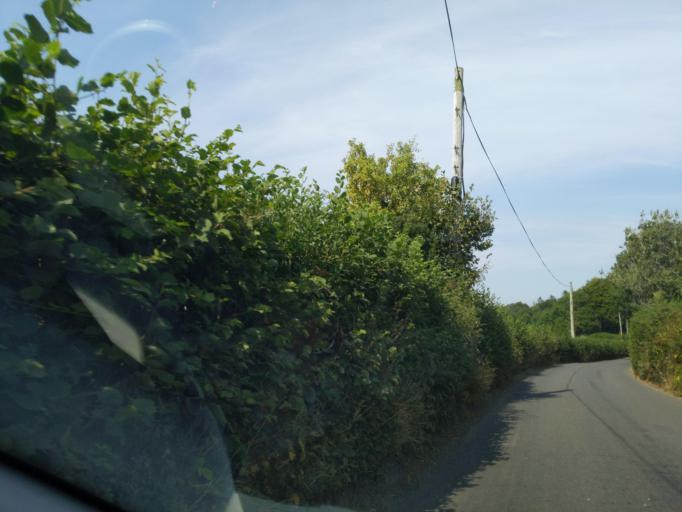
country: GB
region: England
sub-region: Devon
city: Winkleigh
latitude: 50.8766
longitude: -3.8946
